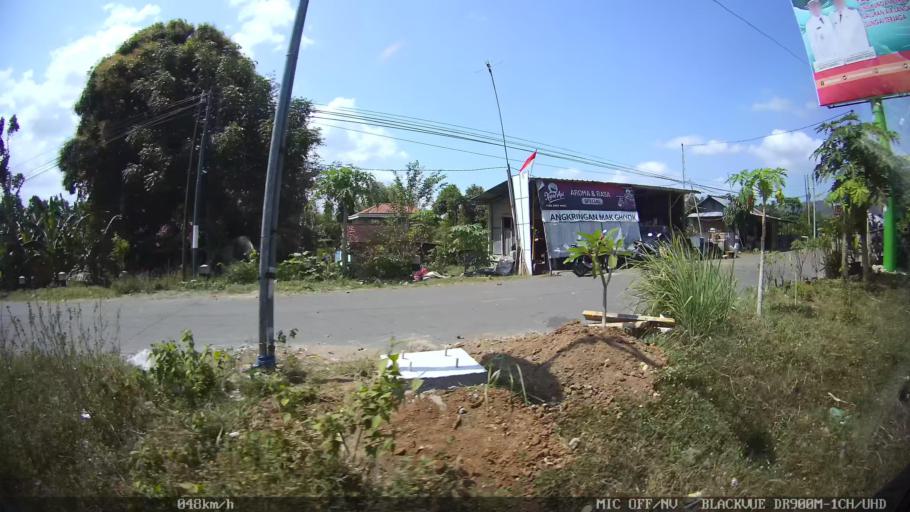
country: ID
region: Daerah Istimewa Yogyakarta
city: Pundong
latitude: -7.9514
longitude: 110.3785
